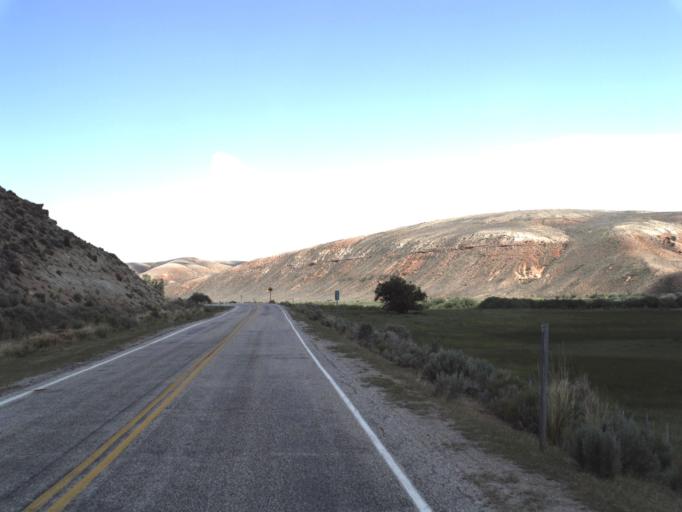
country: US
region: Utah
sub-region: Rich County
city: Randolph
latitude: 41.4967
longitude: -111.2673
